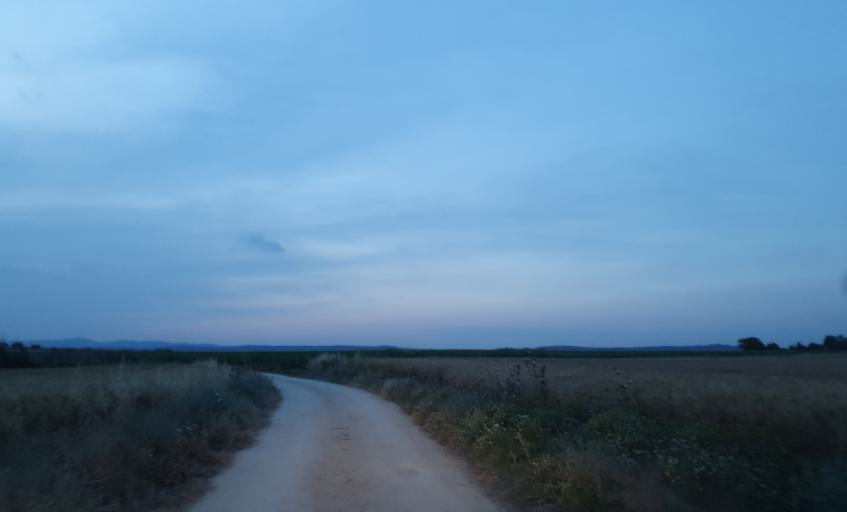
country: TR
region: Kirklareli
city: Vize
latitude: 41.5164
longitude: 27.7451
